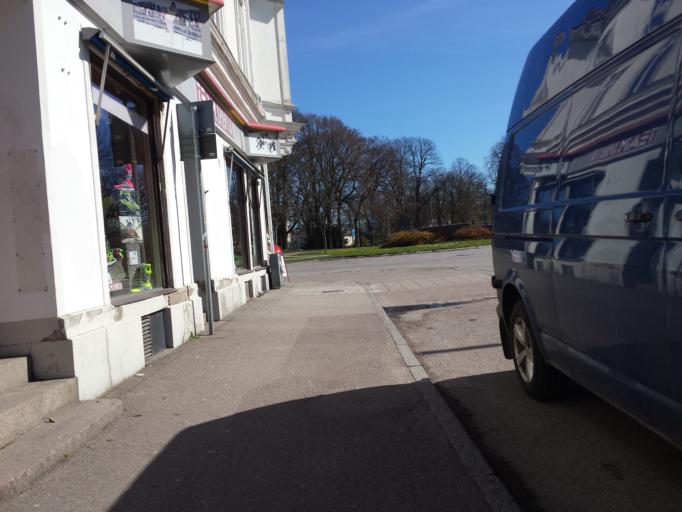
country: SE
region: Kalmar
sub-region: Kalmar Kommun
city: Kalmar
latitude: 56.6631
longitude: 16.3545
